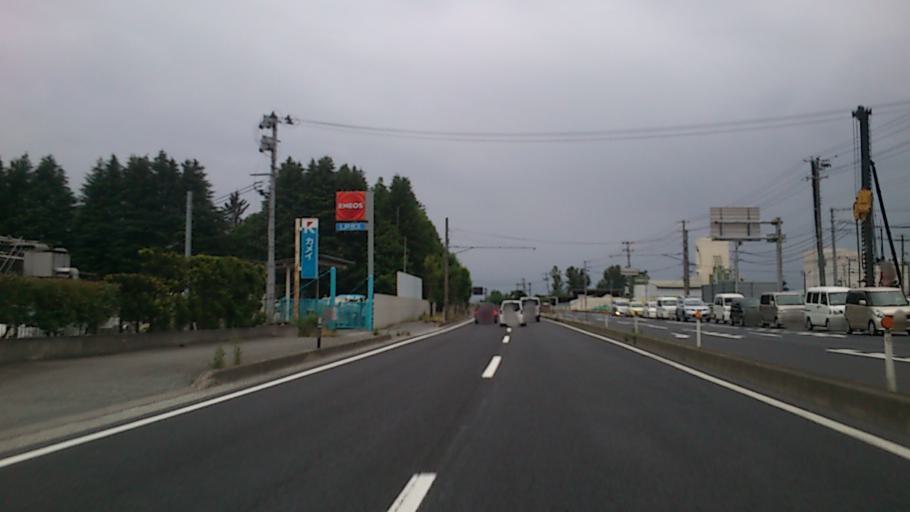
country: JP
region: Yamagata
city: Tendo
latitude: 38.3232
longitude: 140.3637
